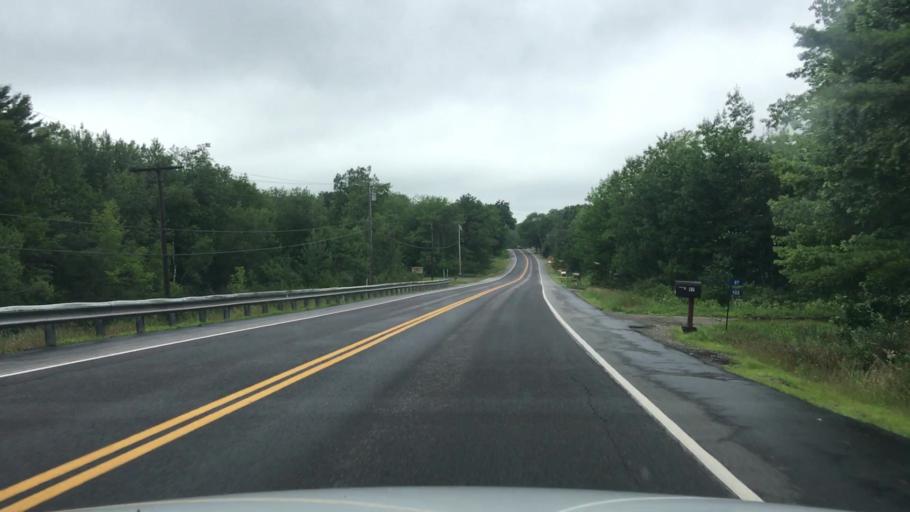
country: US
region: Maine
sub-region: Knox County
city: Hope
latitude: 44.2149
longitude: -69.1859
